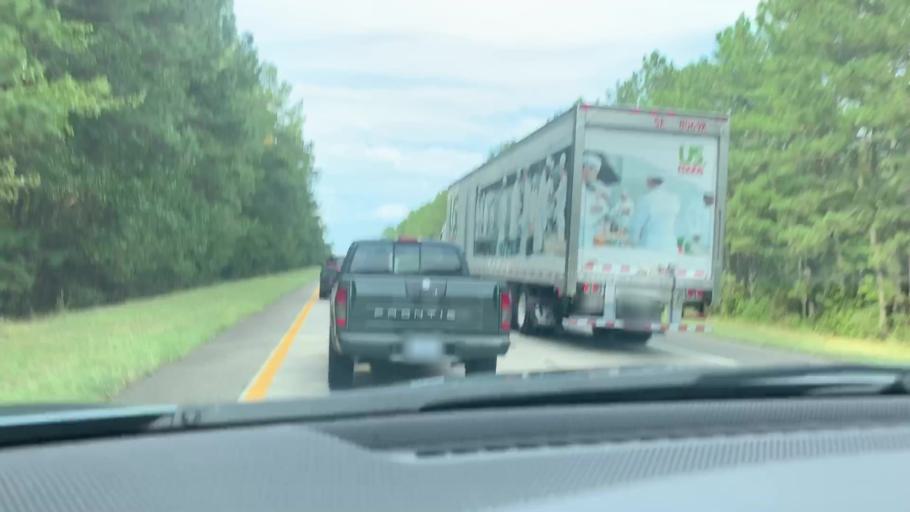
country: US
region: South Carolina
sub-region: Colleton County
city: Walterboro
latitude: 32.9868
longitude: -80.6725
